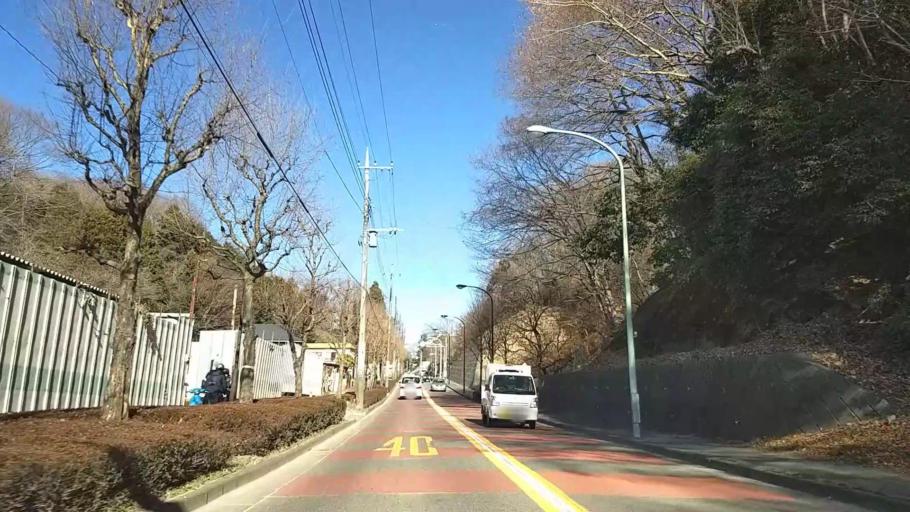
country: JP
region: Tokyo
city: Hachioji
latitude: 35.6200
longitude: 139.2875
